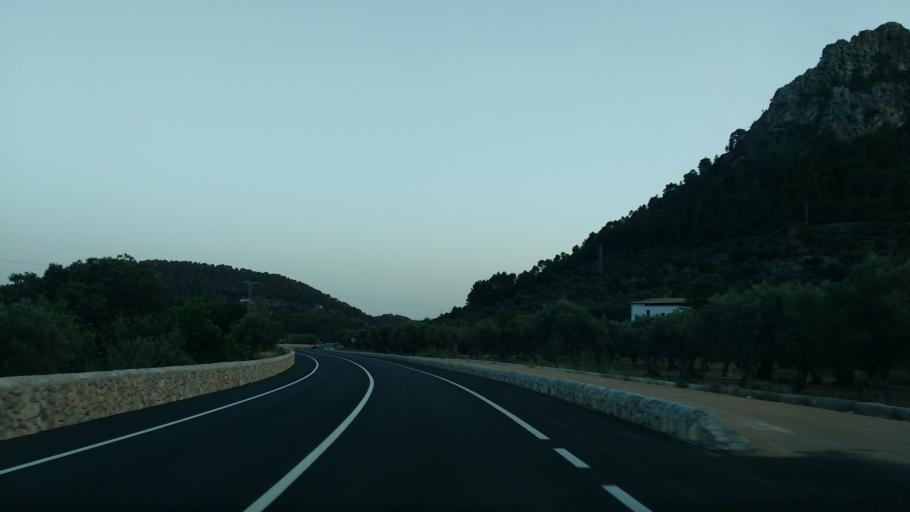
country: ES
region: Balearic Islands
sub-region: Illes Balears
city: Bunyola
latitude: 39.7086
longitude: 2.6889
